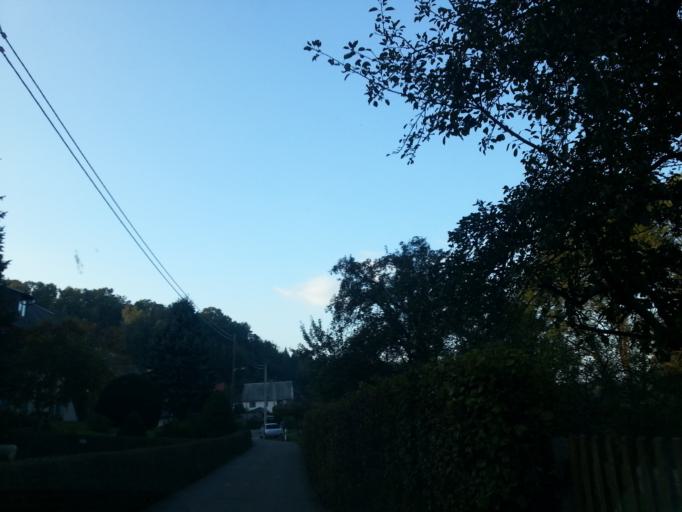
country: DE
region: Saxony
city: Niederschona
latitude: 50.9558
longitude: 13.3959
